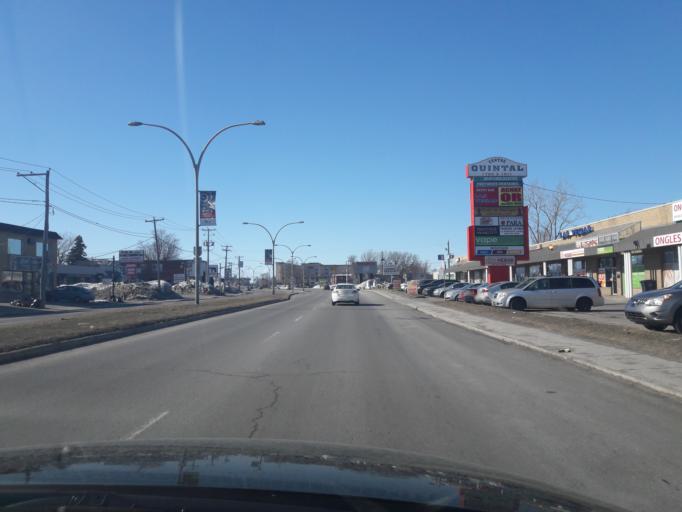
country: CA
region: Quebec
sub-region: Laval
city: Laval
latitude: 45.5525
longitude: -73.7605
